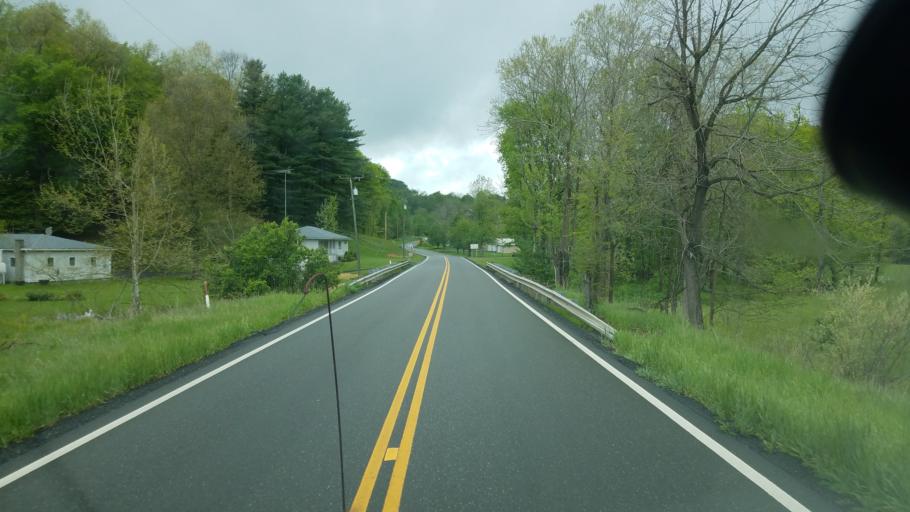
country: US
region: Ohio
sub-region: Harrison County
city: Cadiz
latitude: 40.2719
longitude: -80.8491
